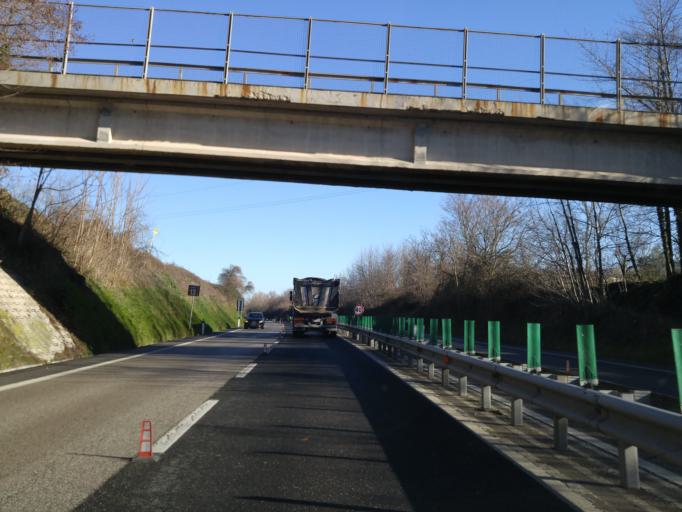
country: IT
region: The Marches
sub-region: Provincia di Pesaro e Urbino
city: Sant'Ippolito
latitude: 43.6912
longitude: 12.8576
